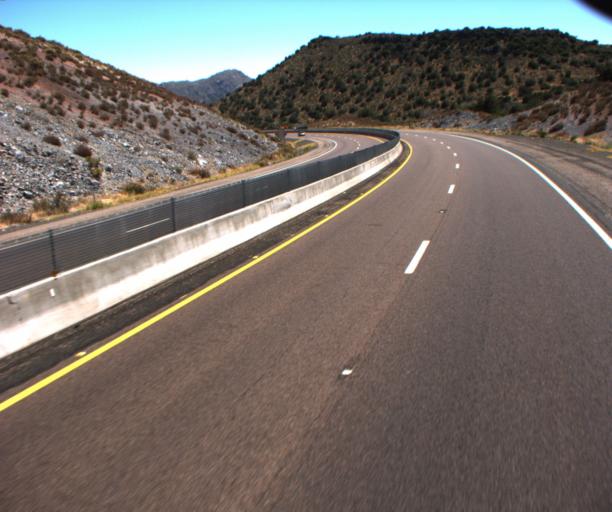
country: US
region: Arizona
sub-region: Gila County
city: Tonto Basin
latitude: 33.8986
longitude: -111.4578
